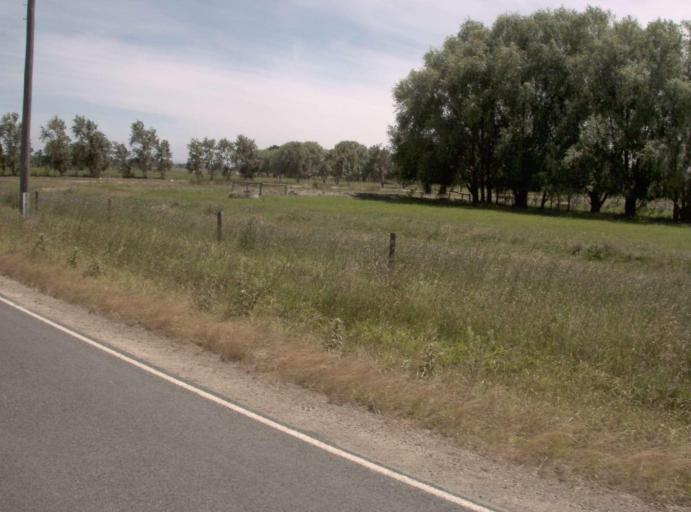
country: AU
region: Victoria
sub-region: Wellington
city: Heyfield
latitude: -38.0553
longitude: 146.8740
